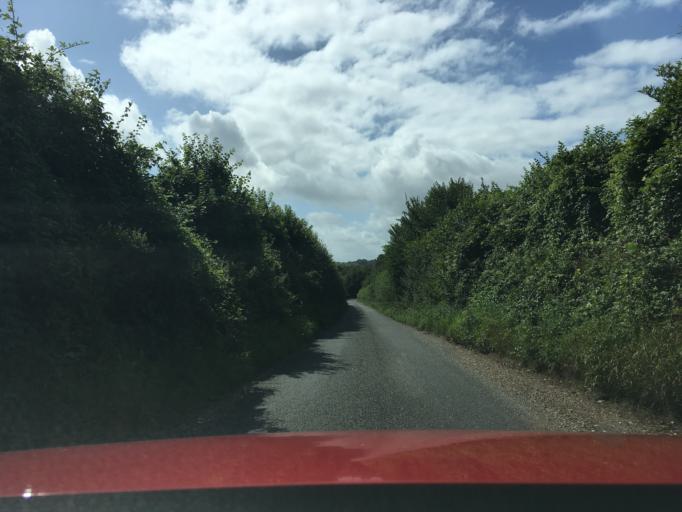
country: GB
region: England
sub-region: West Berkshire
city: Wickham
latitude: 51.4166
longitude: -1.4146
